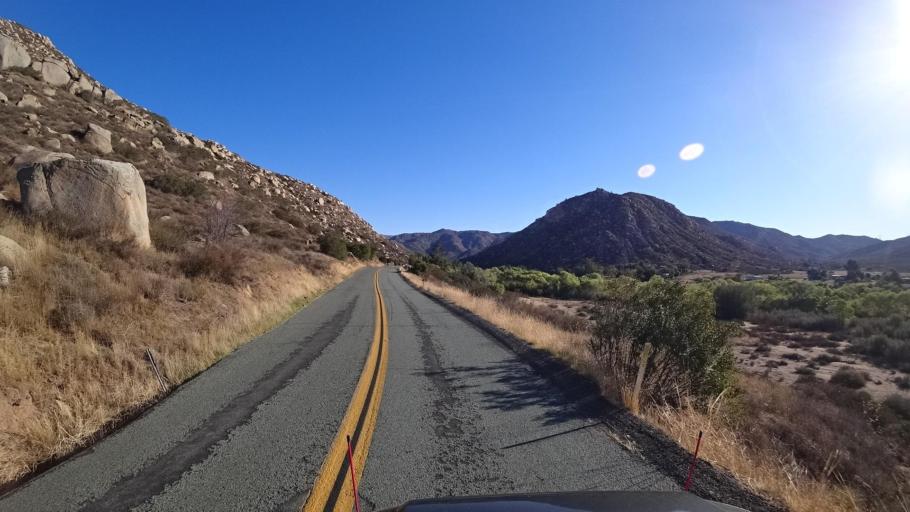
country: MX
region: Baja California
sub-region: Tecate
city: Lomas de Santa Anita
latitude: 32.6155
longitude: -116.6995
